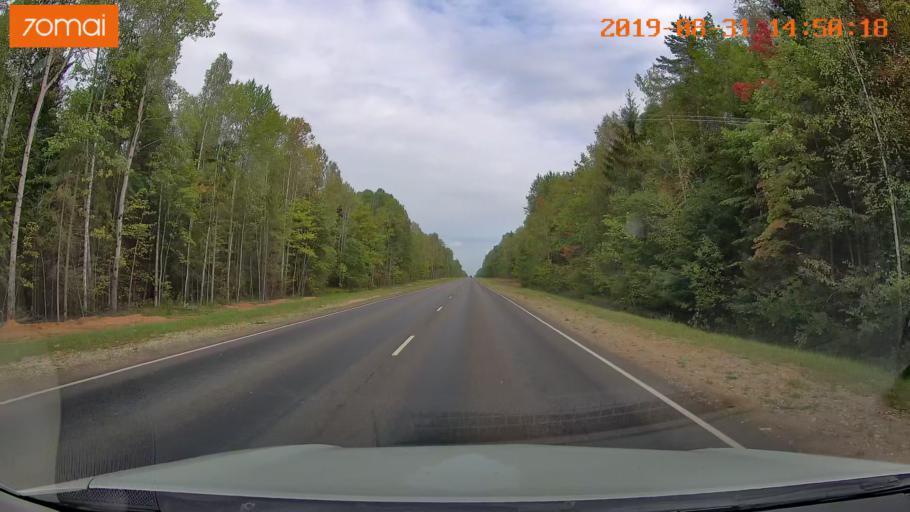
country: RU
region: Kaluga
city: Spas-Demensk
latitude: 54.2602
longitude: 33.7859
